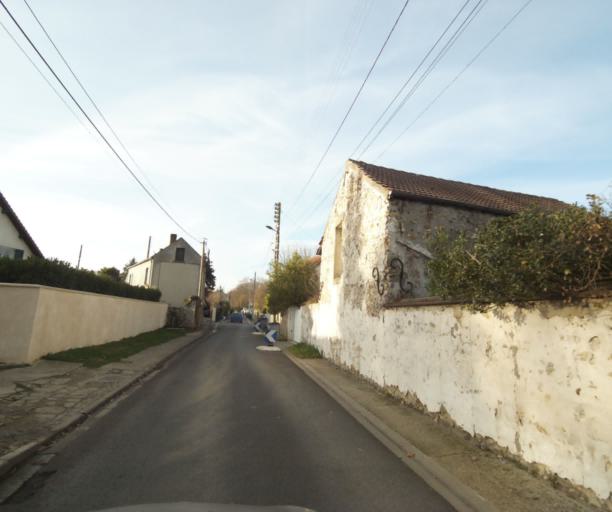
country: FR
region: Ile-de-France
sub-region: Departement des Yvelines
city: Triel-sur-Seine
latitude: 49.0005
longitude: 2.0164
